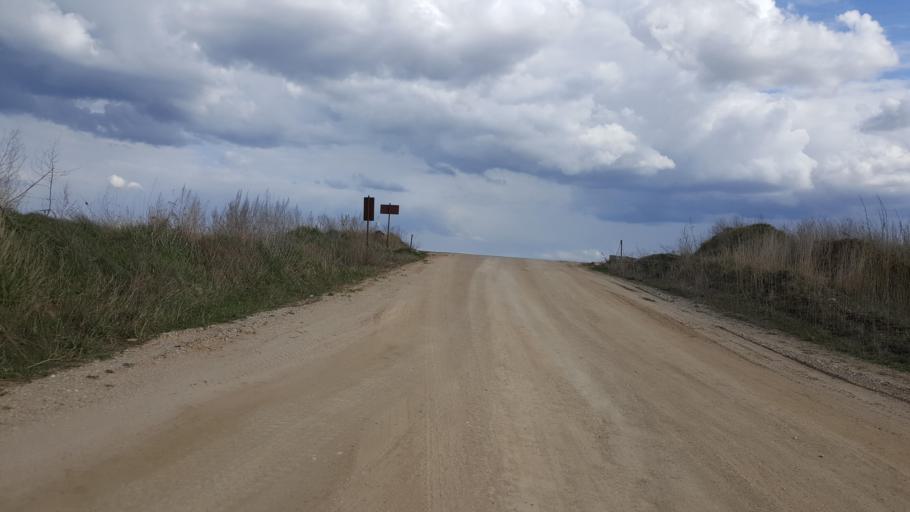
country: BY
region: Brest
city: Kamyanyets
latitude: 52.4395
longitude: 23.6515
